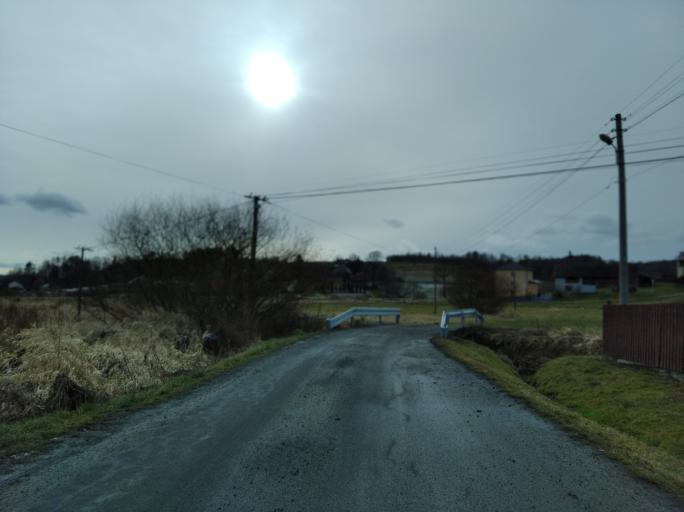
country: PL
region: Subcarpathian Voivodeship
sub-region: Powiat strzyzowski
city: Strzyzow
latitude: 49.9031
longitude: 21.7390
